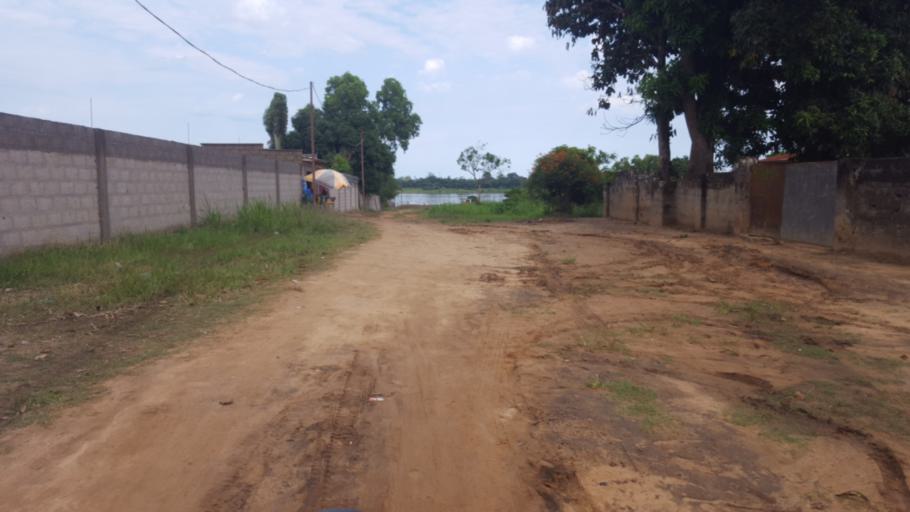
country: CD
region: Bandundu
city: Bandundu
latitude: -3.3020
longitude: 17.3708
